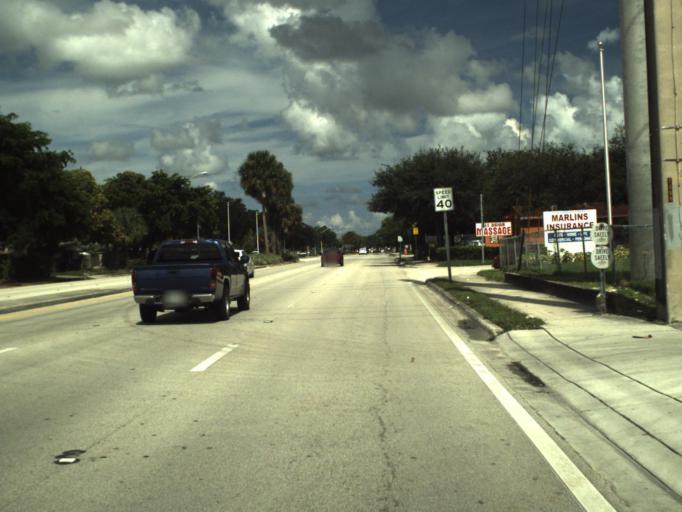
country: US
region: Florida
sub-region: Broward County
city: Pembroke Pines
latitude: 26.0321
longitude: -80.2073
